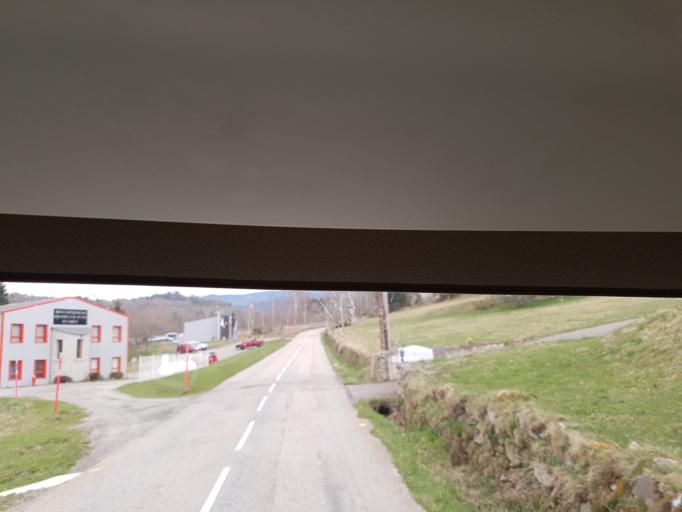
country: FR
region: Languedoc-Roussillon
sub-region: Departement de l'Aude
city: Quillan
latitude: 42.7119
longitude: 2.0825
